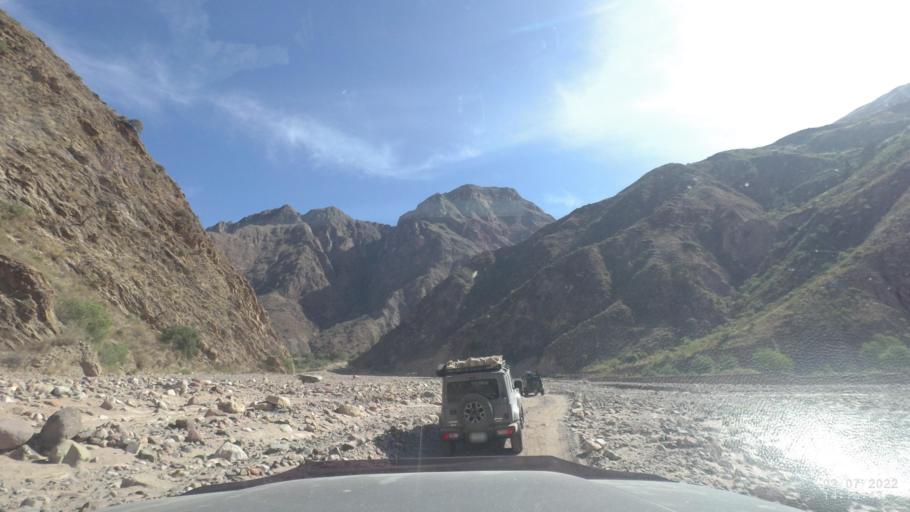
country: BO
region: Cochabamba
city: Irpa Irpa
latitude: -17.8273
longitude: -66.4085
